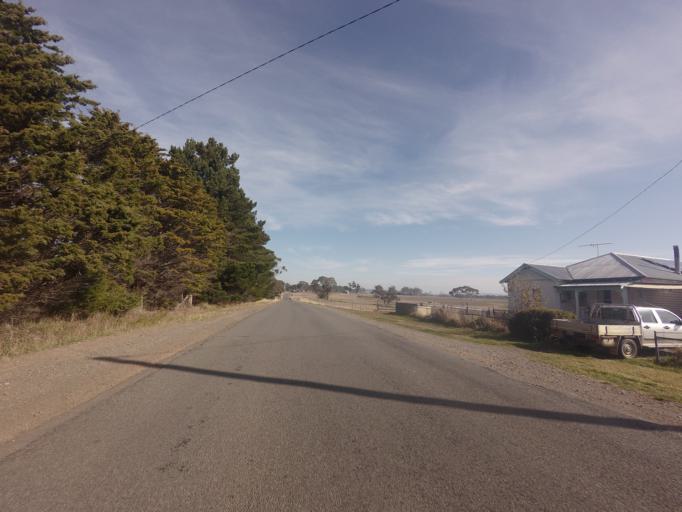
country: AU
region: Tasmania
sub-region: Sorell
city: Sorell
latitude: -42.4428
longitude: 147.4691
